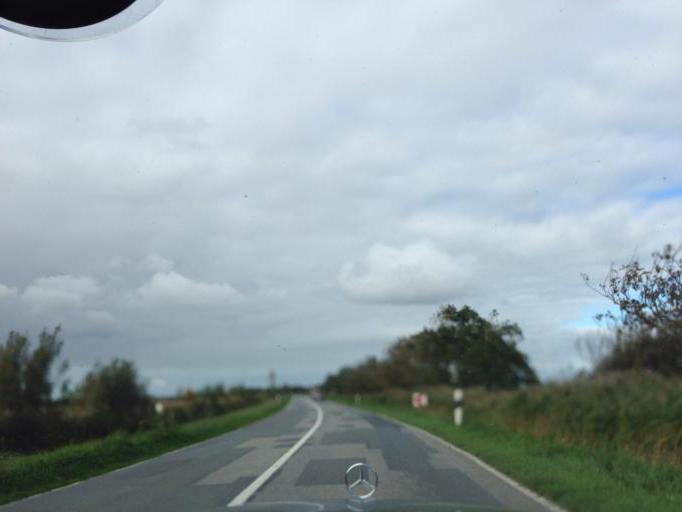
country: DE
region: Schleswig-Holstein
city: Galmsbull
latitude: 54.7538
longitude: 8.7524
